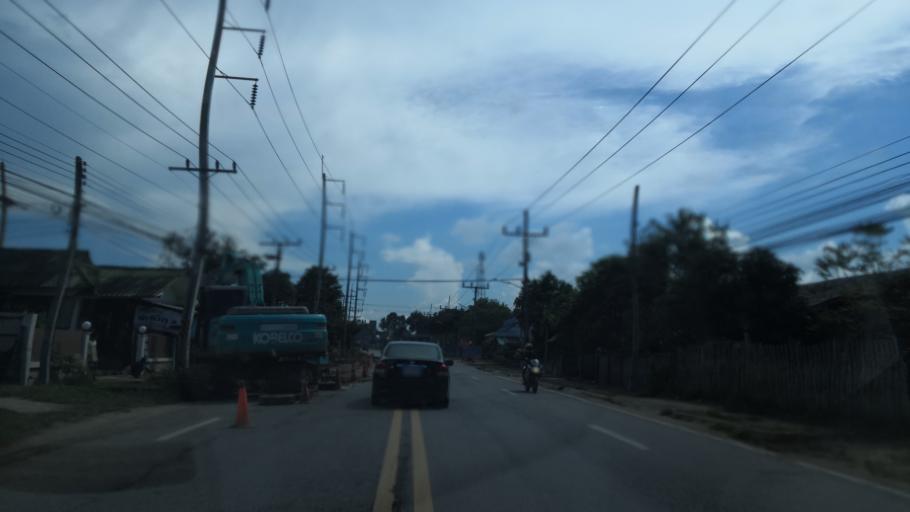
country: TH
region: Chiang Rai
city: Wiang Pa Pao
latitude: 19.3753
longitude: 99.5024
